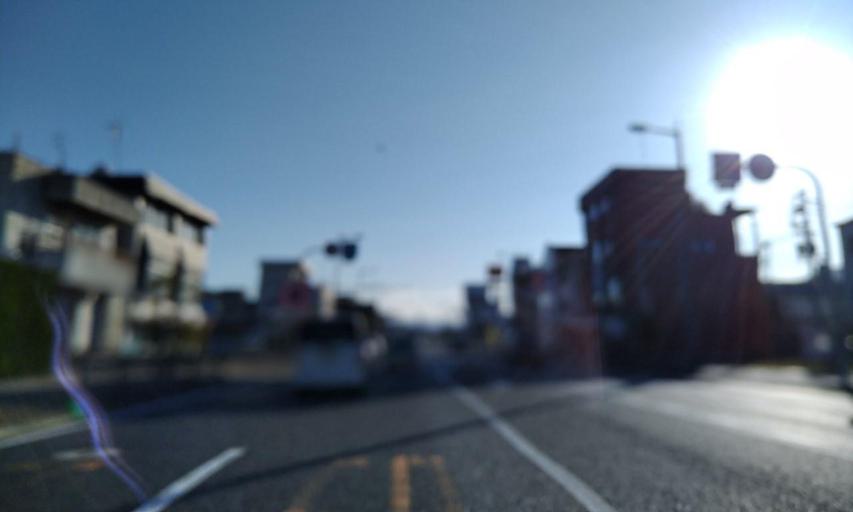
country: JP
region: Wakayama
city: Kainan
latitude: 34.1588
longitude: 135.2025
